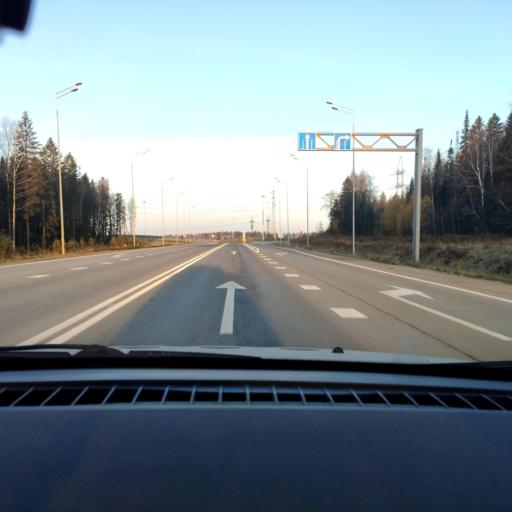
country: RU
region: Perm
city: Novyye Lyady
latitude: 58.0436
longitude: 56.4417
